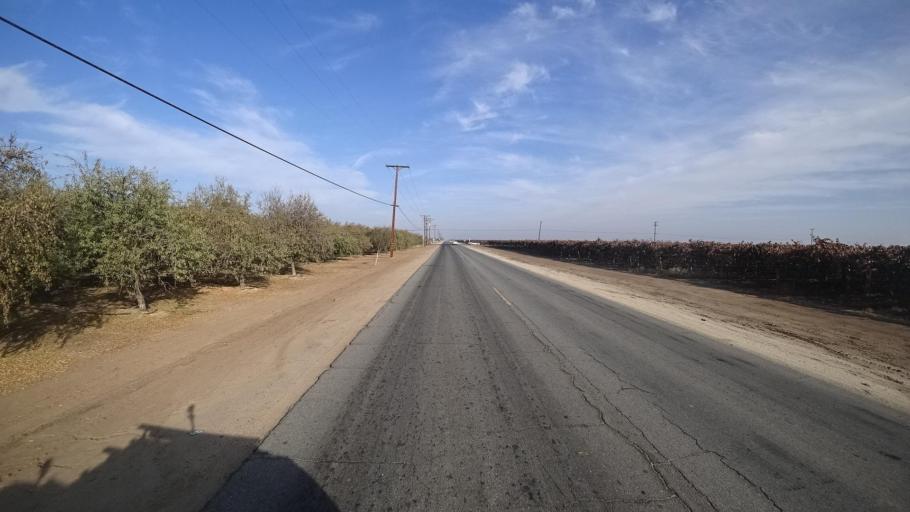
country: US
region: California
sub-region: Kern County
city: McFarland
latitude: 35.6733
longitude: -119.2047
